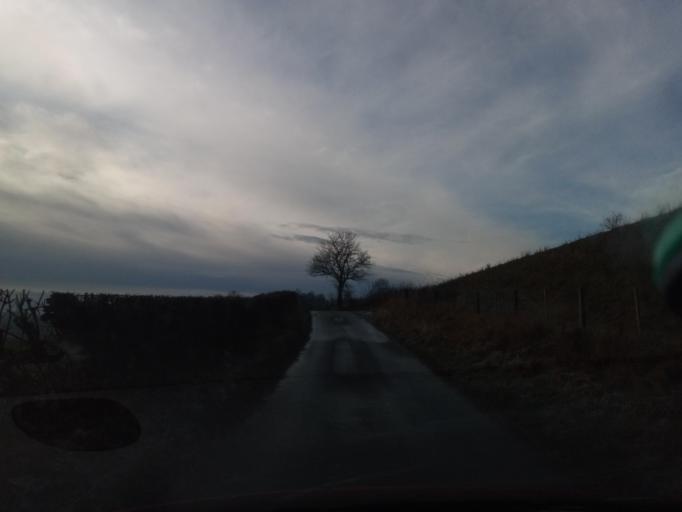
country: GB
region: Scotland
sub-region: The Scottish Borders
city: Hawick
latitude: 55.4461
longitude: -2.7454
